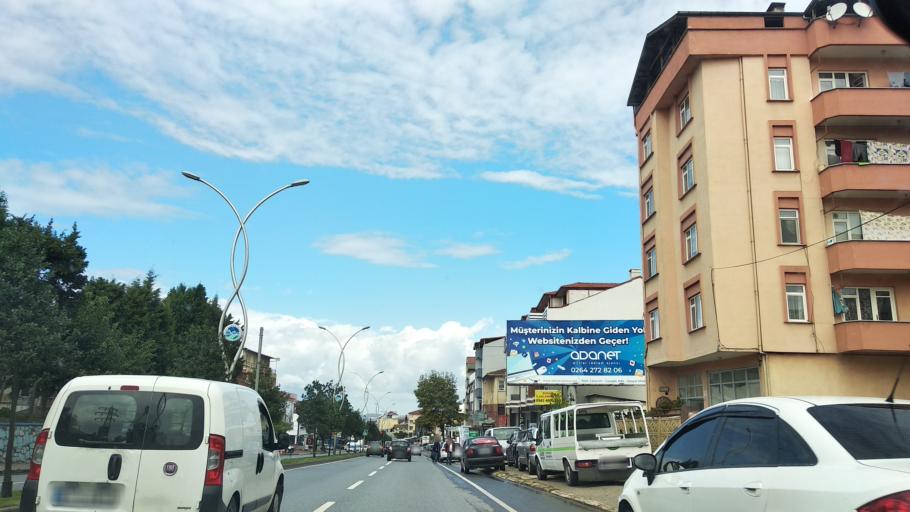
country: TR
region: Sakarya
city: Adapazari
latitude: 40.7481
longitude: 30.3863
